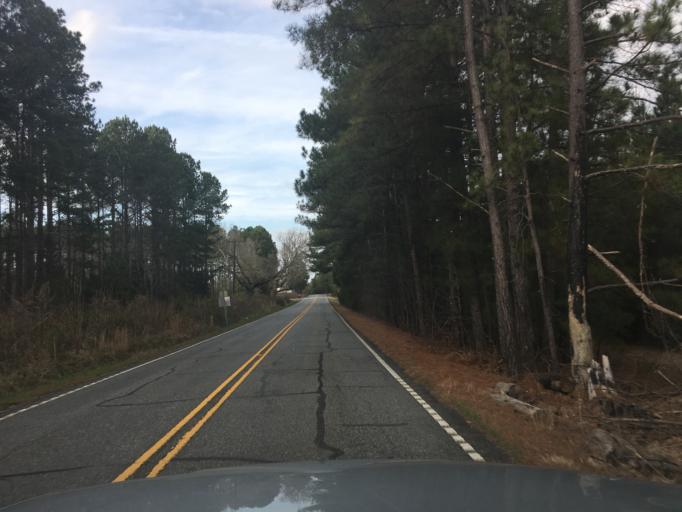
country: US
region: South Carolina
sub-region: Abbeville County
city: Lake Secession
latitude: 34.3668
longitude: -82.5200
